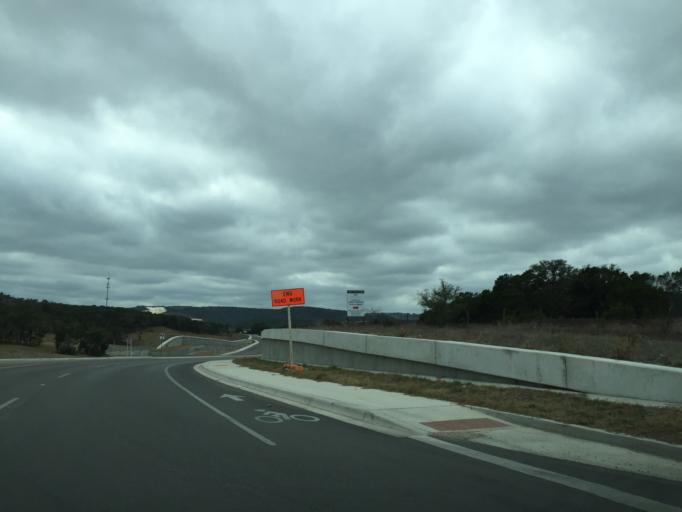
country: US
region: Texas
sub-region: Travis County
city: The Hills
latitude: 30.3427
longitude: -98.0260
